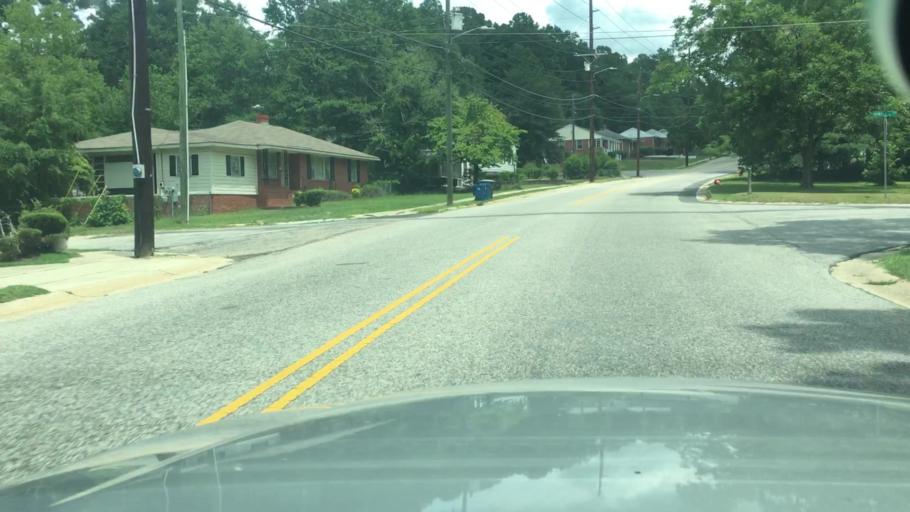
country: US
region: North Carolina
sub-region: Cumberland County
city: Fayetteville
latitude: 35.0799
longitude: -78.8877
